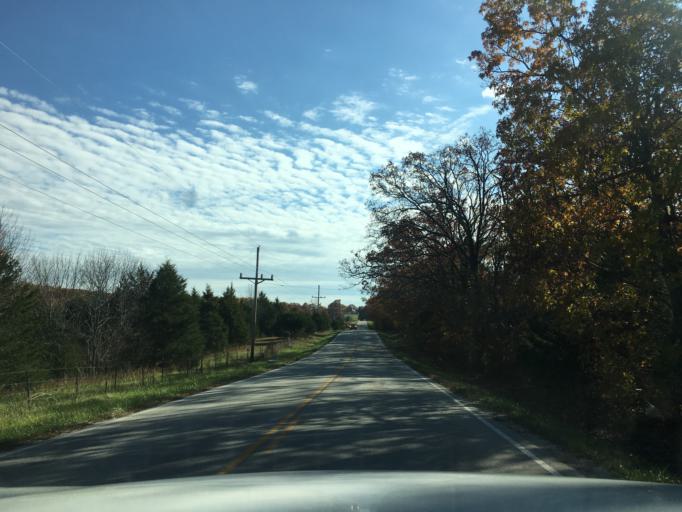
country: US
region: Missouri
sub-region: Maries County
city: Belle
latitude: 38.3315
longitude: -91.7624
